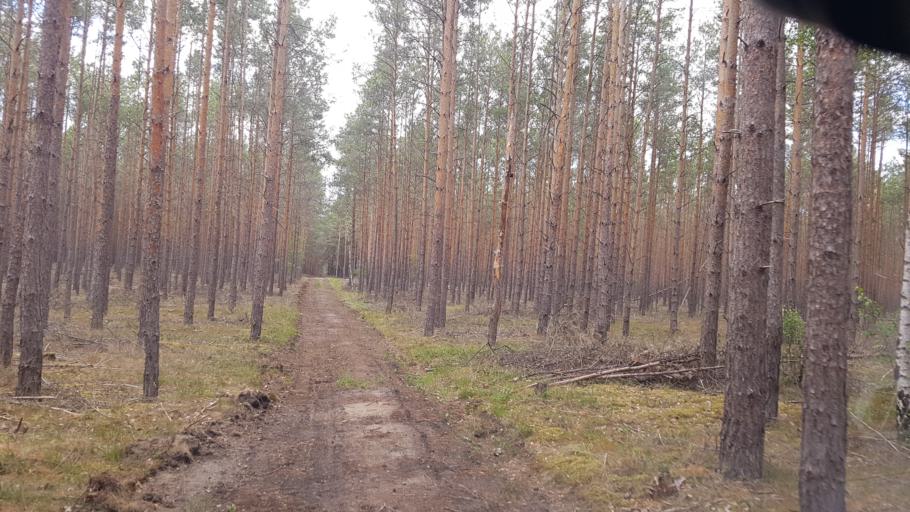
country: DE
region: Brandenburg
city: Finsterwalde
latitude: 51.6195
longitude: 13.6590
